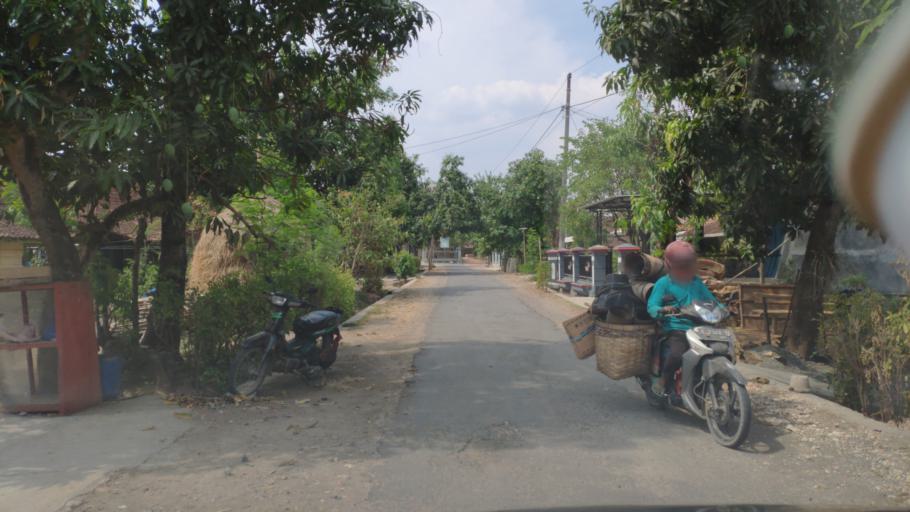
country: ID
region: Central Java
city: Gotputuk
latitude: -6.9893
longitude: 111.3062
